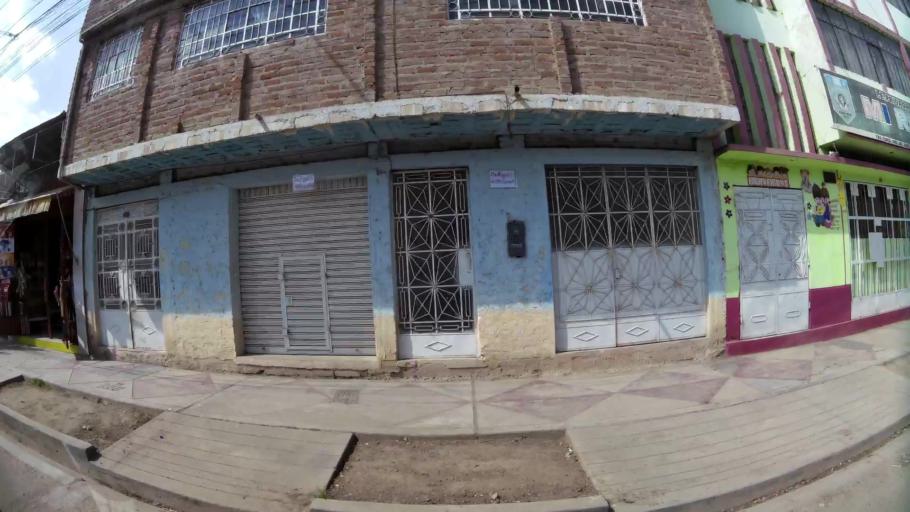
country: PE
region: Junin
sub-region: Provincia de Huancayo
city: Huancayo
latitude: -12.0861
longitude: -75.2063
